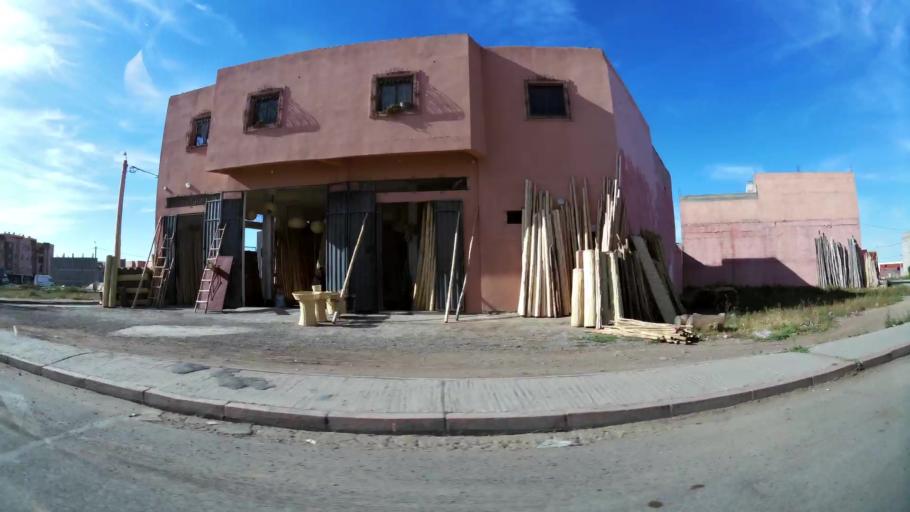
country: MA
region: Marrakech-Tensift-Al Haouz
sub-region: Marrakech
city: Marrakesh
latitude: 31.6827
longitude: -8.0600
